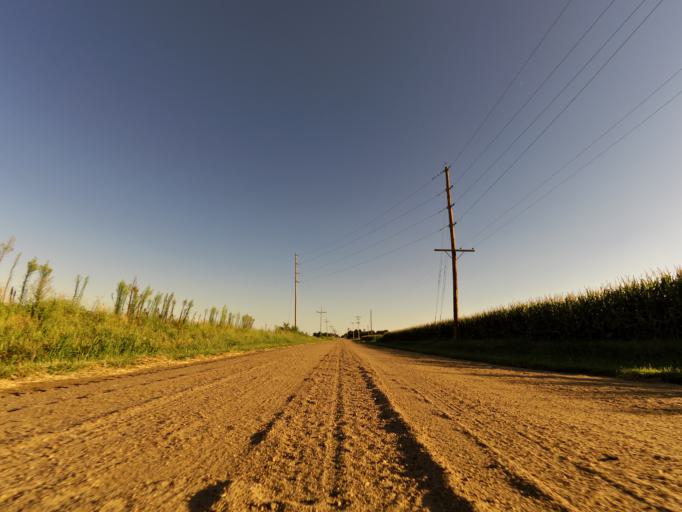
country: US
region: Kansas
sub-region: Reno County
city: South Hutchinson
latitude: 38.0044
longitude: -98.0319
